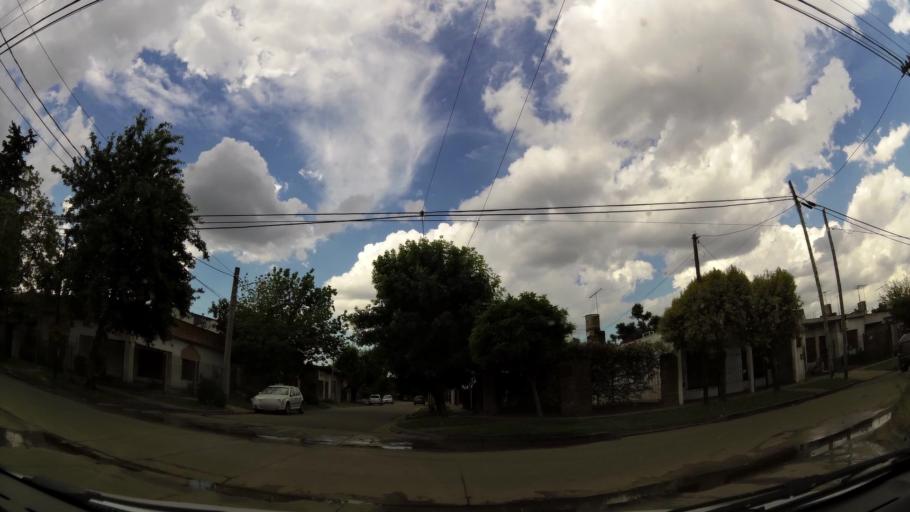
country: AR
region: Buenos Aires
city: Ituzaingo
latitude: -34.6371
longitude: -58.6733
